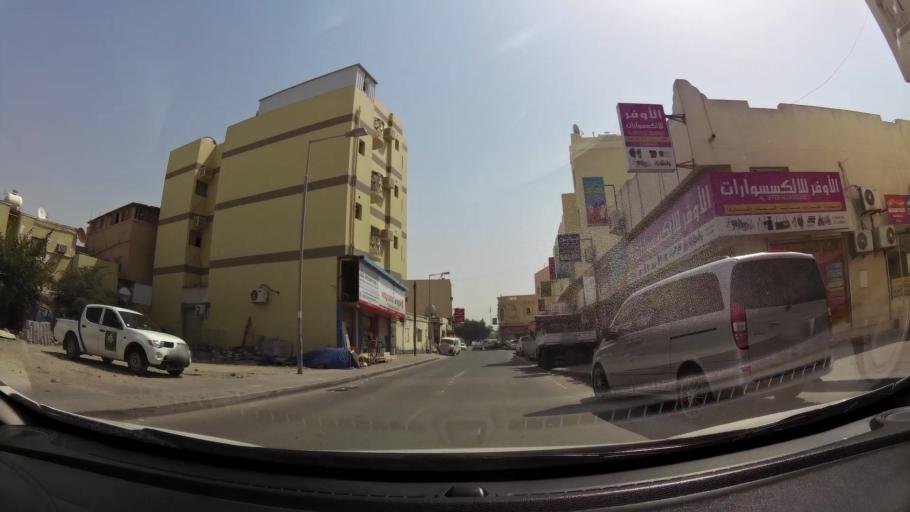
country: BH
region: Manama
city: Jidd Hafs
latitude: 26.2146
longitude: 50.4505
